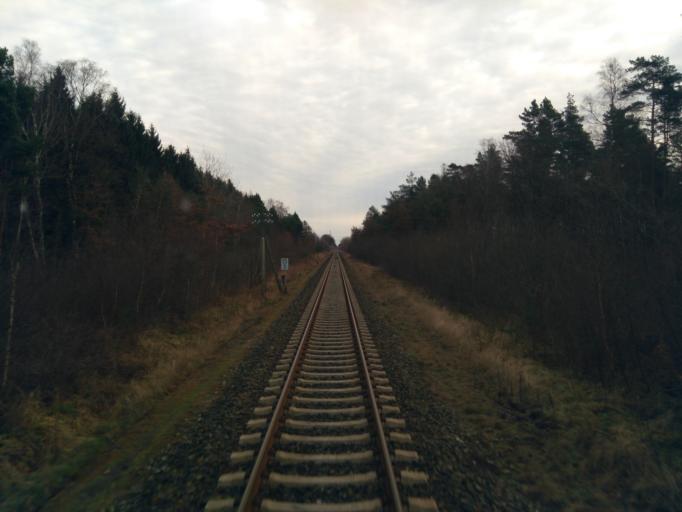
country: DE
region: Lower Saxony
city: Hanstedt Eins
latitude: 53.0116
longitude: 10.3610
